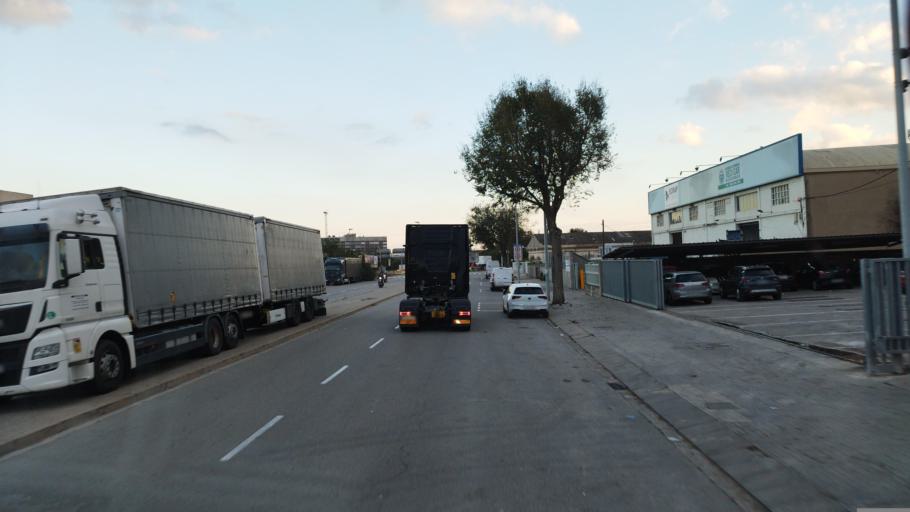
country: ES
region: Catalonia
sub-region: Provincia de Barcelona
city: Sants-Montjuic
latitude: 41.3500
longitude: 2.1363
